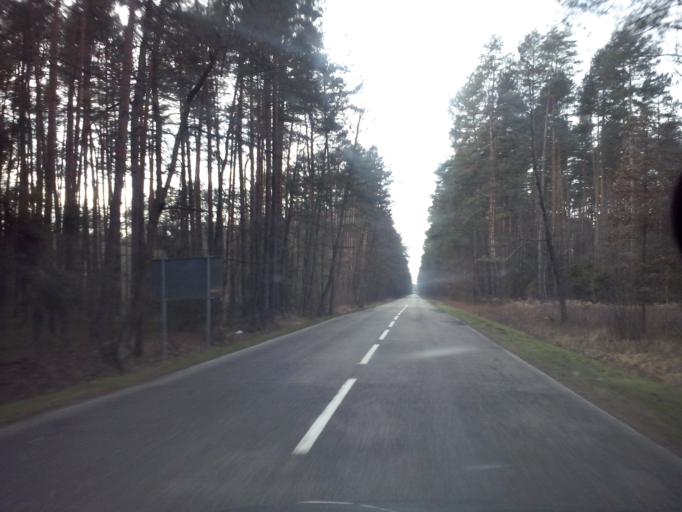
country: PL
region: Subcarpathian Voivodeship
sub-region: Powiat nizanski
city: Harasiuki
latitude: 50.4710
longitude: 22.4601
